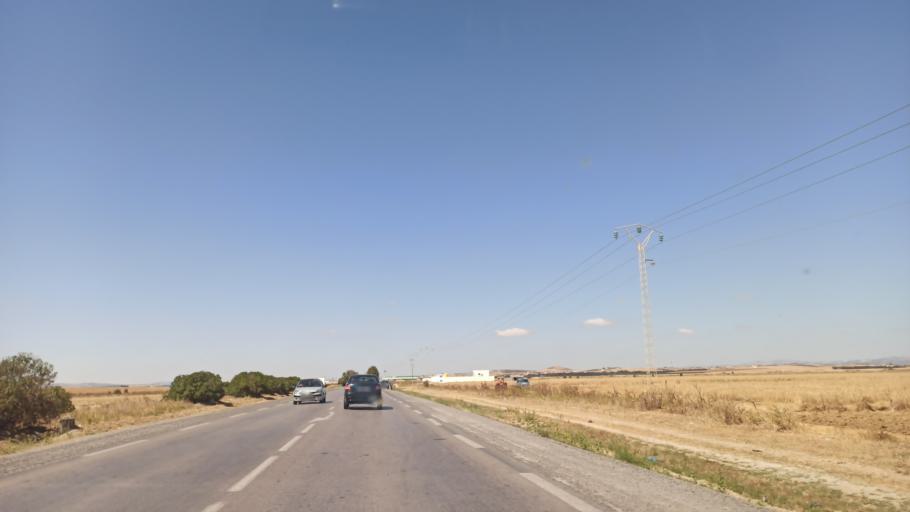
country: TN
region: Tunis
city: Oued Lill
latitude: 36.7456
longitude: 9.9647
